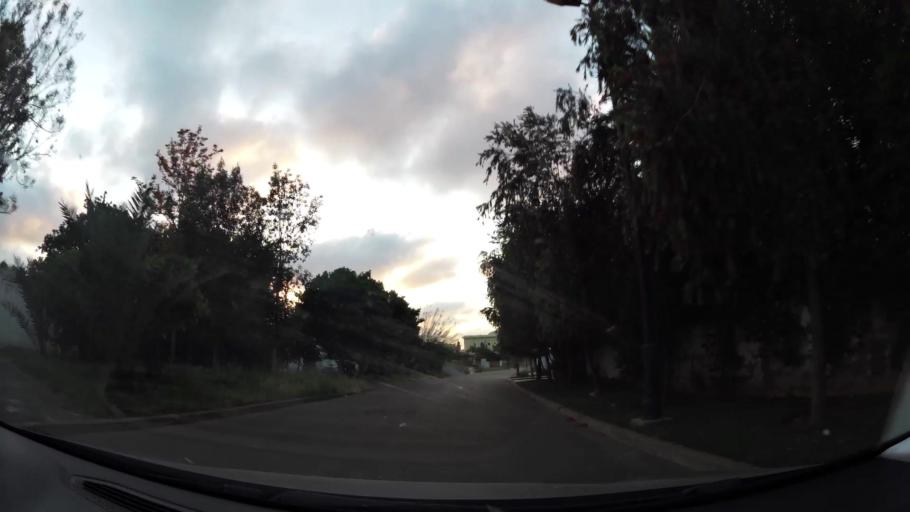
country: MA
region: Rabat-Sale-Zemmour-Zaer
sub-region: Rabat
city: Rabat
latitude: 33.9672
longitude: -6.8368
